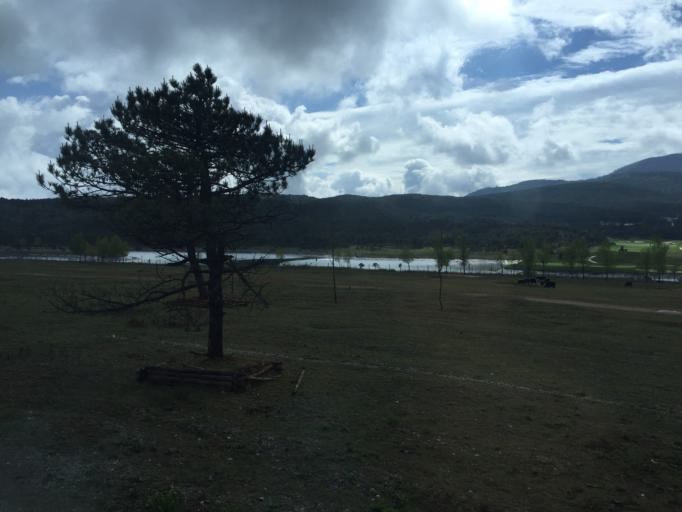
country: CN
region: Yunnan
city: Xiaqiaotou
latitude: 27.1099
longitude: 100.2516
